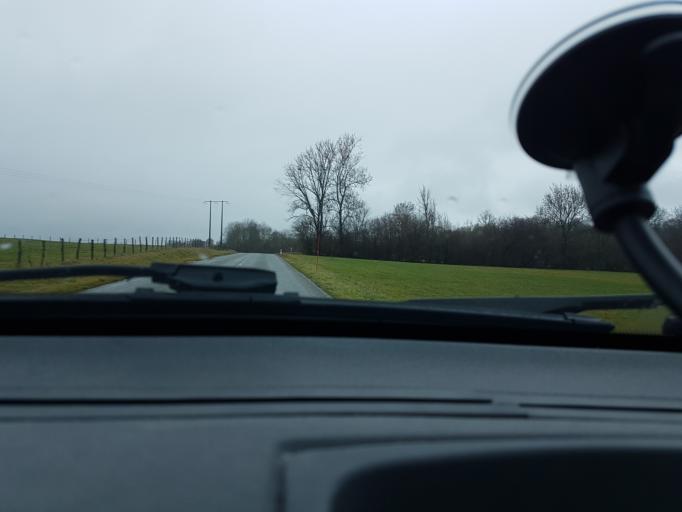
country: FR
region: Franche-Comte
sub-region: Departement du Doubs
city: Valdahon
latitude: 47.1044
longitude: 6.3568
